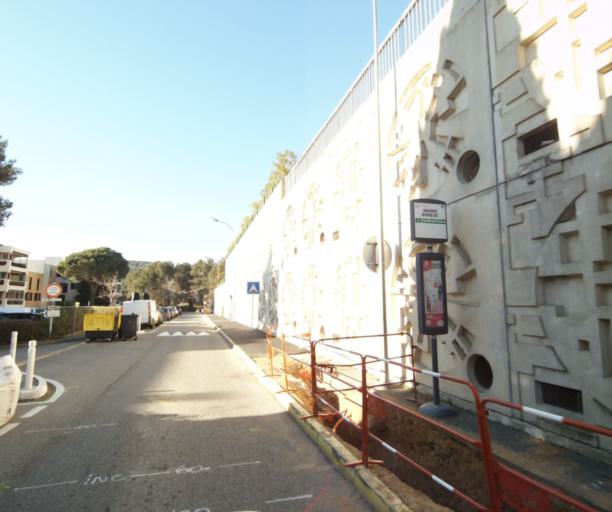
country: FR
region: Provence-Alpes-Cote d'Azur
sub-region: Departement des Alpes-Maritimes
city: Vallauris
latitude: 43.5967
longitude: 7.0696
